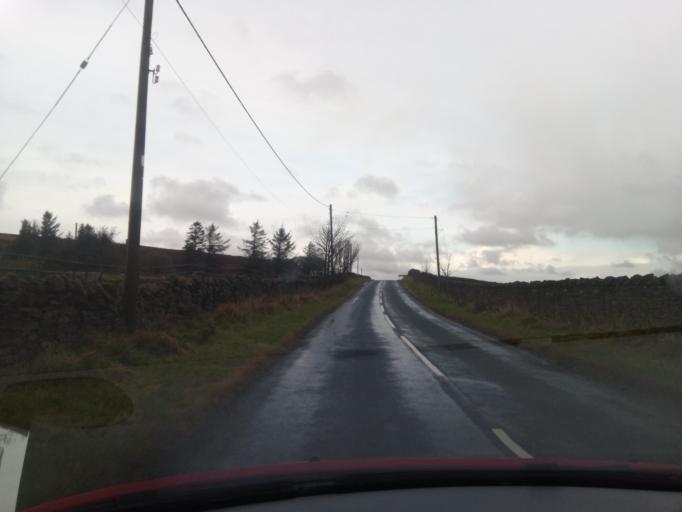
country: GB
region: England
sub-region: County Durham
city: Muggleswick
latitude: 54.8473
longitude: -1.9801
